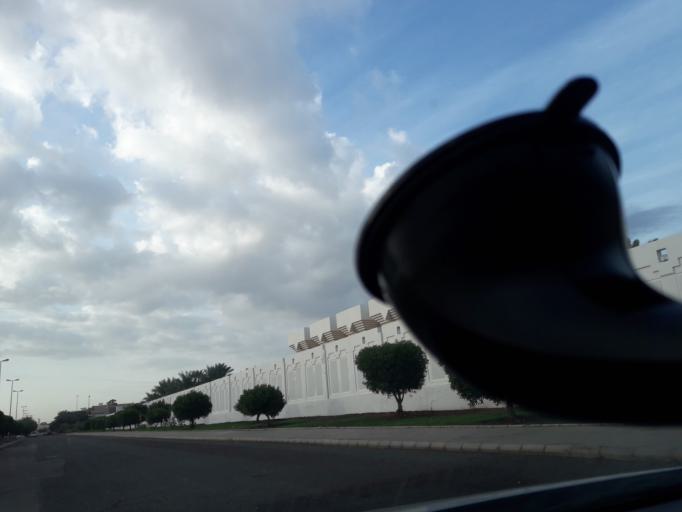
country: SA
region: Al Madinah al Munawwarah
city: Medina
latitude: 24.4262
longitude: 39.6269
